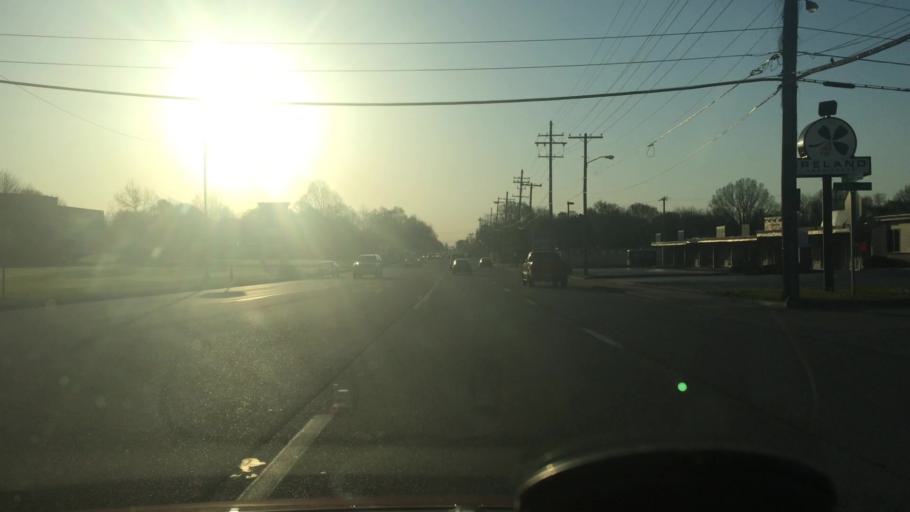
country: US
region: Missouri
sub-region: Greene County
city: Springfield
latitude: 37.1815
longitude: -93.2604
